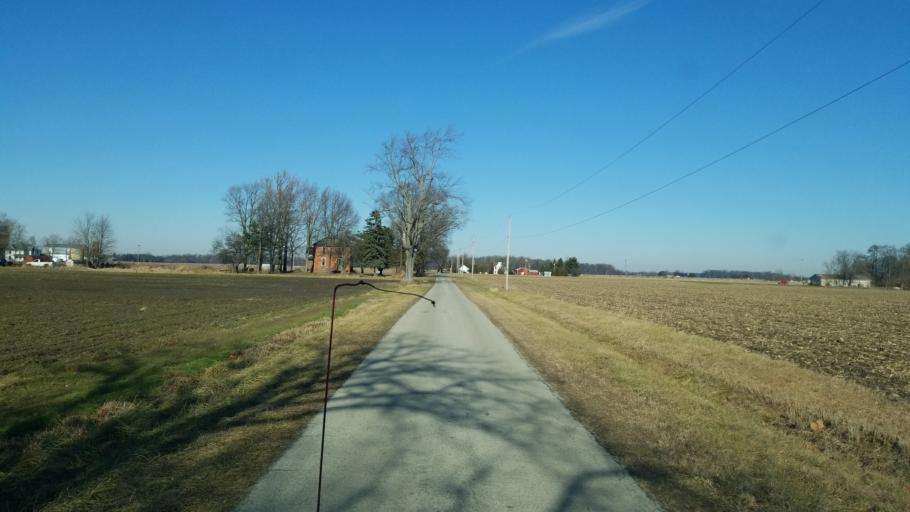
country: US
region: Ohio
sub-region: Henry County
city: Liberty Center
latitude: 41.3683
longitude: -83.9802
